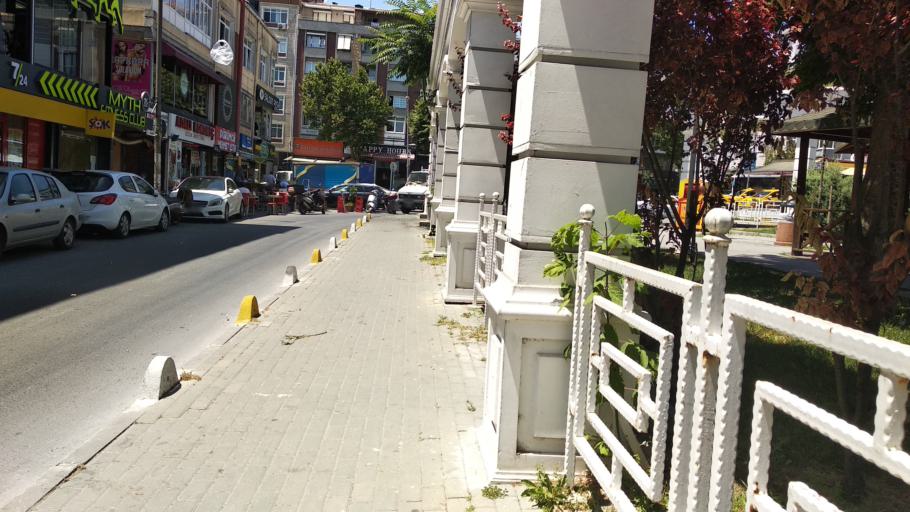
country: TR
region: Istanbul
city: Yakuplu
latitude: 40.9776
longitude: 28.7204
